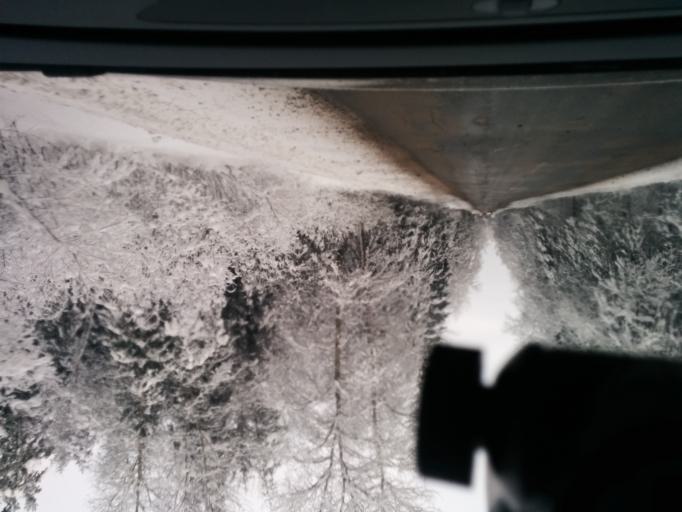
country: LV
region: Ogre
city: Ogre
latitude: 56.8314
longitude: 24.5882
